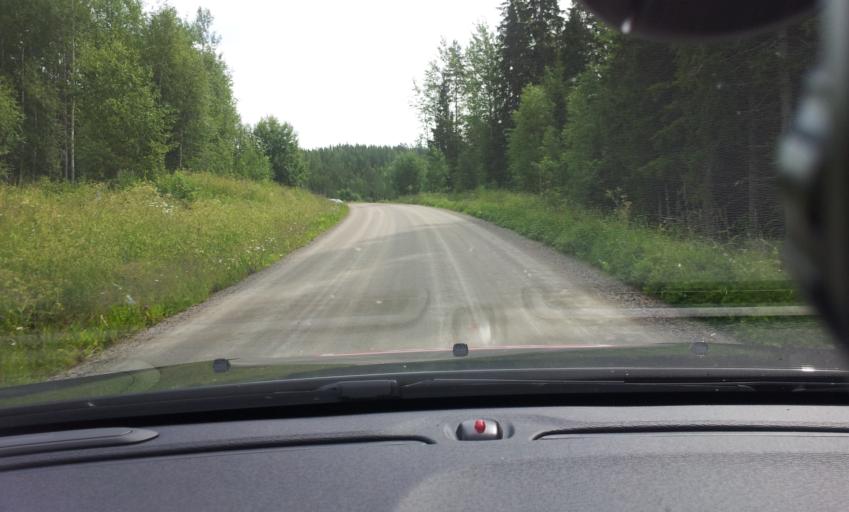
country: SE
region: Jaemtland
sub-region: OEstersunds Kommun
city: Brunflo
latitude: 62.9395
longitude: 14.9604
